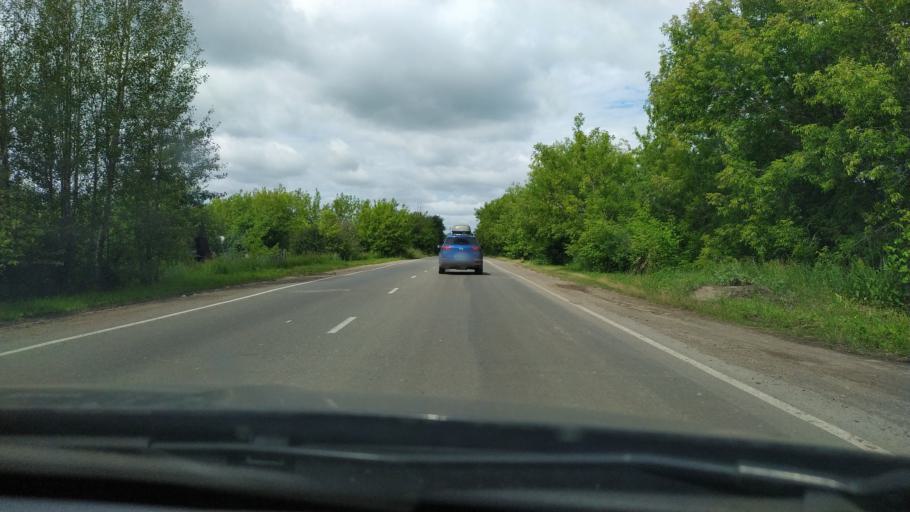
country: RU
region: Perm
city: Kondratovo
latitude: 57.9287
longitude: 56.1083
